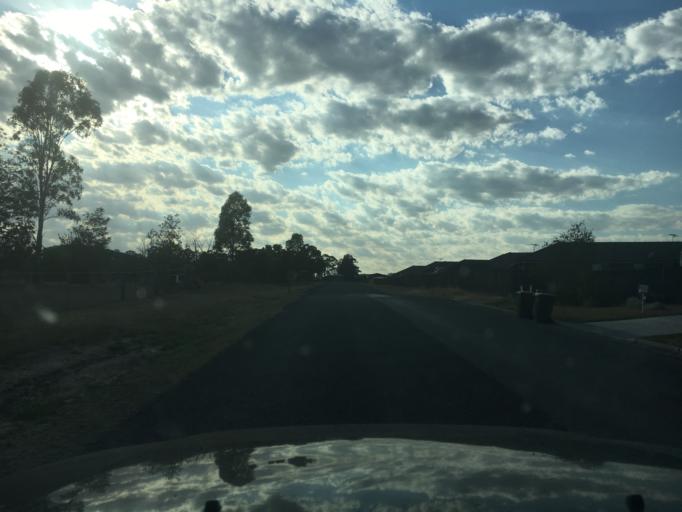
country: AU
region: New South Wales
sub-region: Cessnock
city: Branxton
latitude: -32.6518
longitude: 151.3685
